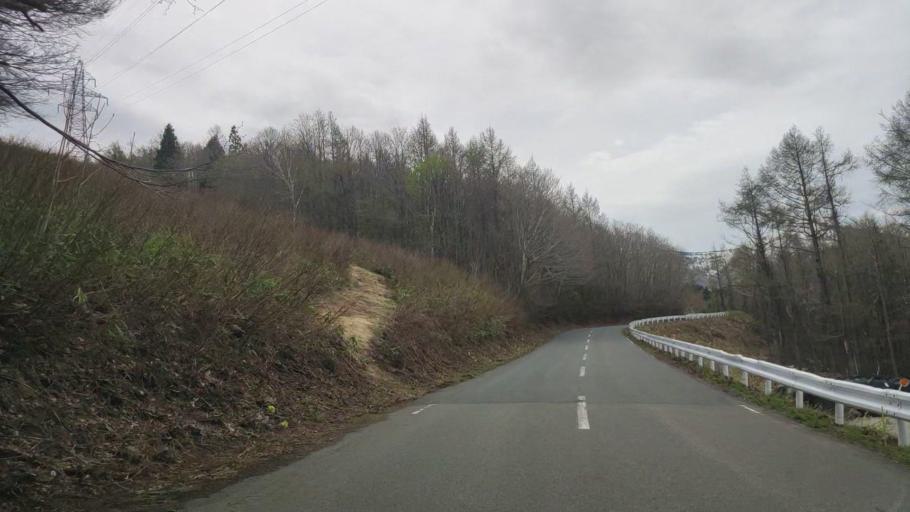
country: JP
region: Aomori
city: Aomori Shi
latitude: 40.7173
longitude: 140.8681
